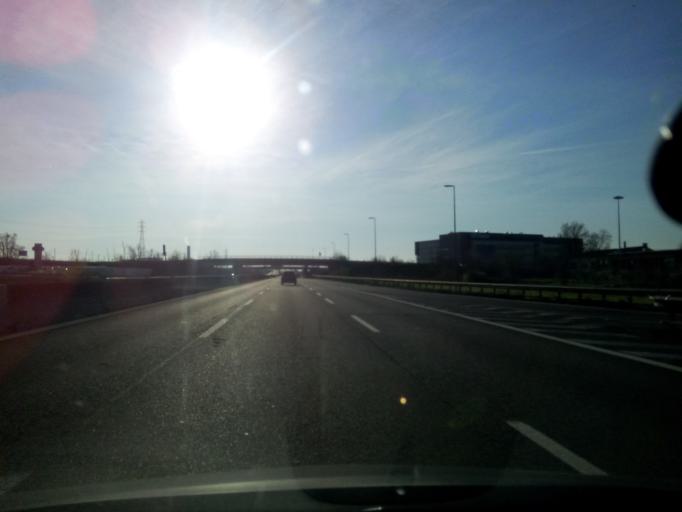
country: IT
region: Emilia-Romagna
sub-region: Provincia di Parma
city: Baganzola
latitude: 44.8401
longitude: 10.3378
